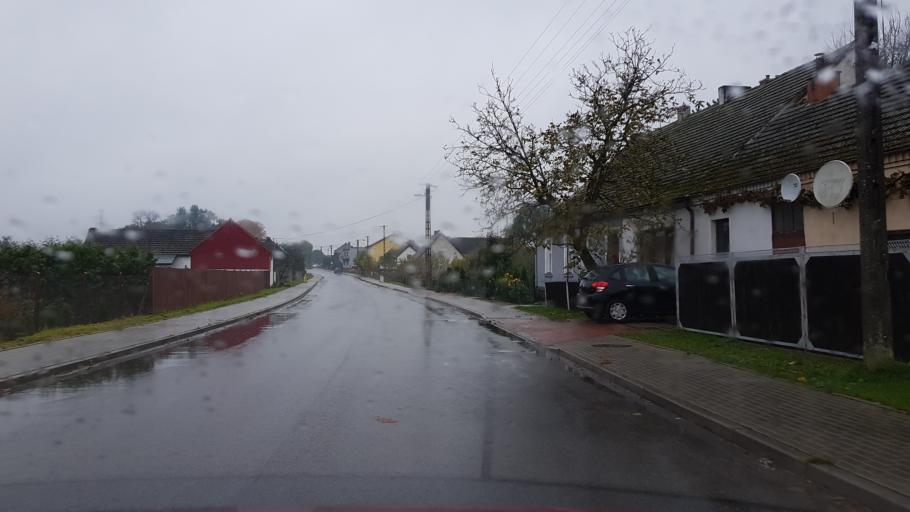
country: PL
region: Greater Poland Voivodeship
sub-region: Powiat zlotowski
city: Tarnowka
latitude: 53.3404
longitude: 16.8580
